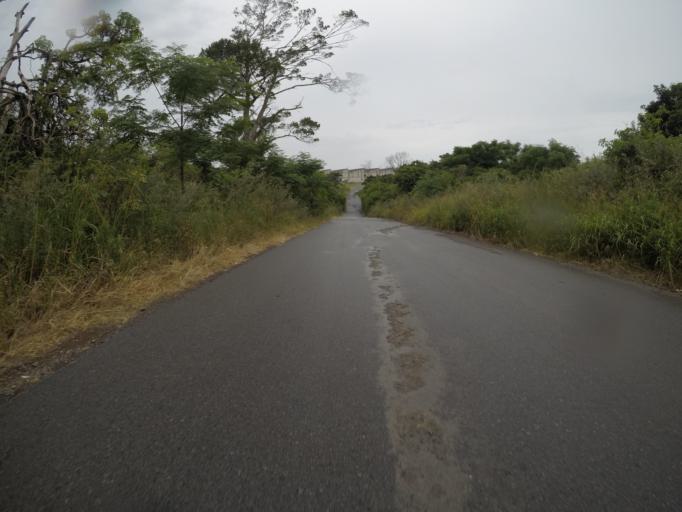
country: ZA
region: Eastern Cape
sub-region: Buffalo City Metropolitan Municipality
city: East London
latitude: -32.9678
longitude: 27.8179
